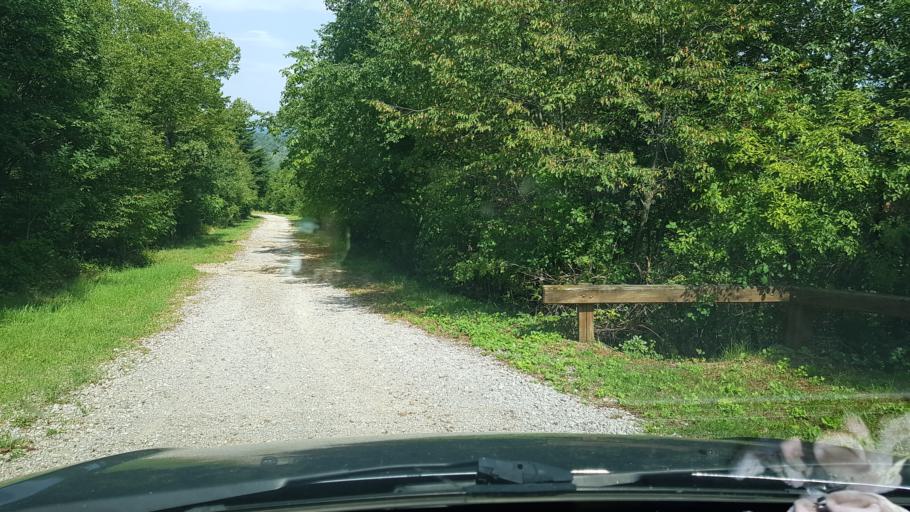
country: SI
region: Nova Gorica
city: Solkan
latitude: 46.0011
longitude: 13.6538
